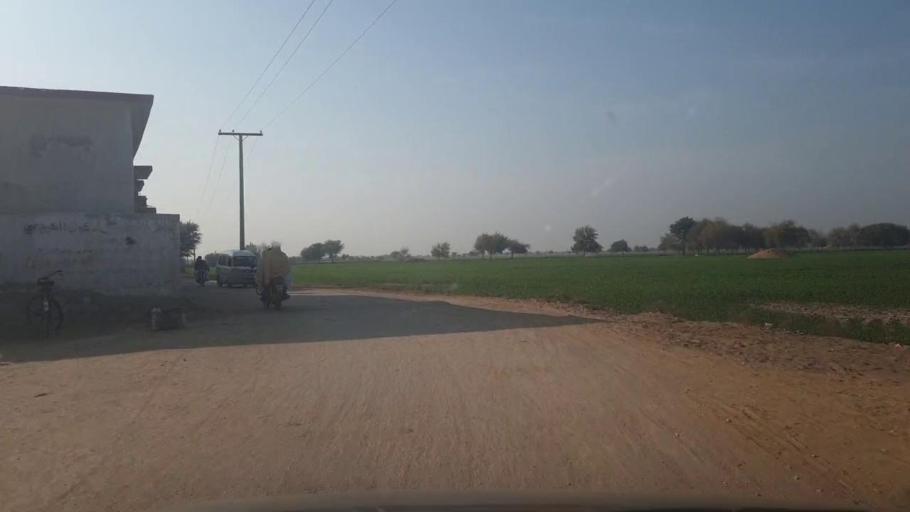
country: PK
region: Sindh
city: Sakrand
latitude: 26.0541
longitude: 68.3958
